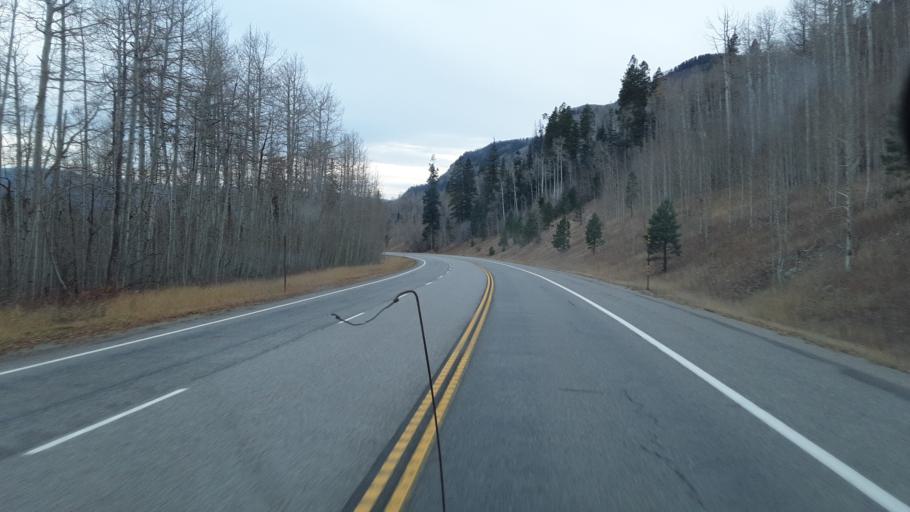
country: US
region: Colorado
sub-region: San Juan County
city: Silverton
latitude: 37.5688
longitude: -107.8248
